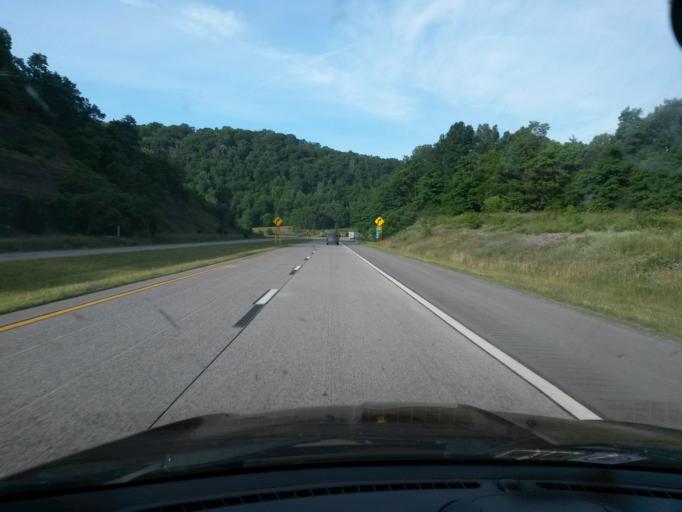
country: US
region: West Virginia
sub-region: Summers County
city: Hinton
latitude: 37.7886
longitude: -80.8765
